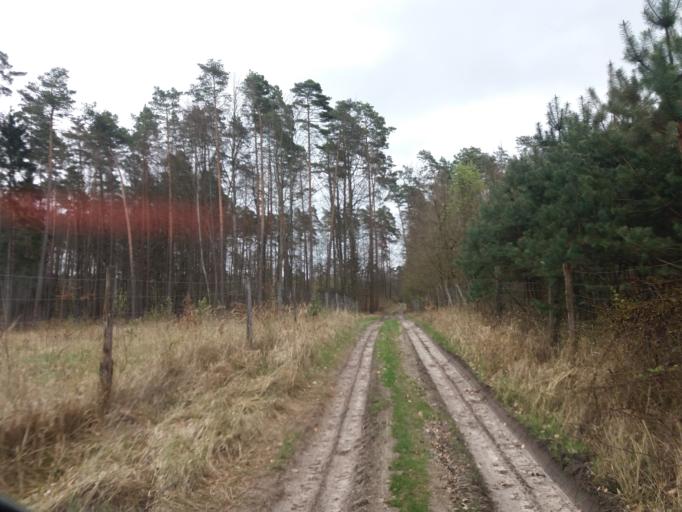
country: PL
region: West Pomeranian Voivodeship
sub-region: Powiat choszczenski
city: Drawno
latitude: 53.1120
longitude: 15.8422
